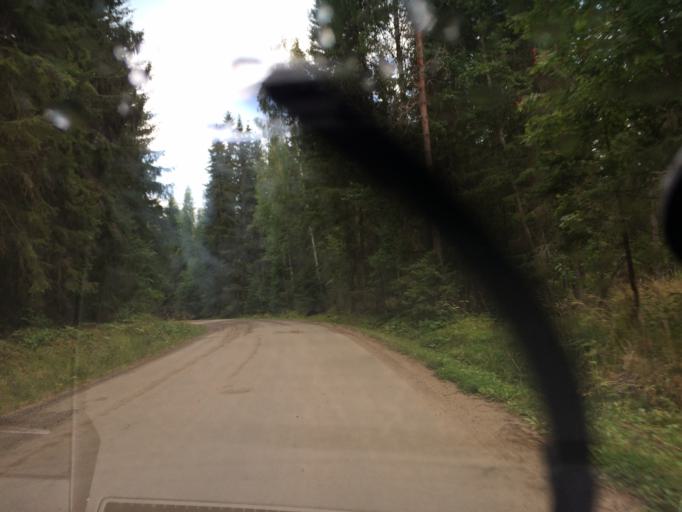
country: FI
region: Pirkanmaa
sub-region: Tampere
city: Luopioinen
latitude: 61.2726
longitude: 24.6726
